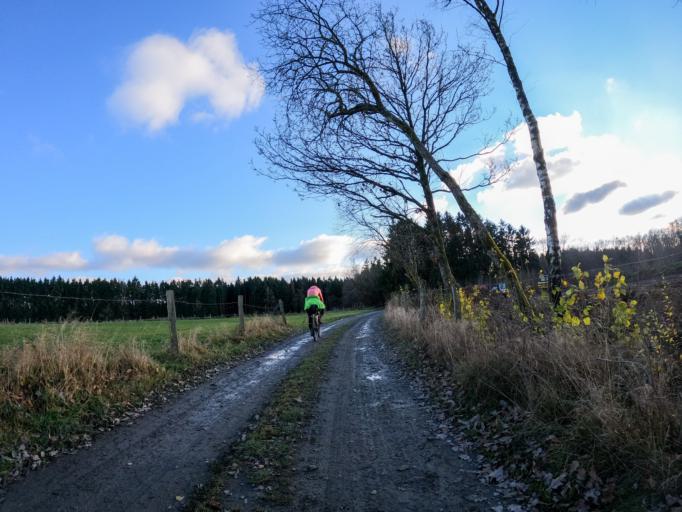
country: LU
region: Diekirch
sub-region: Canton de Wiltz
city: Bavigne
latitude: 49.9793
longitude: 5.8289
